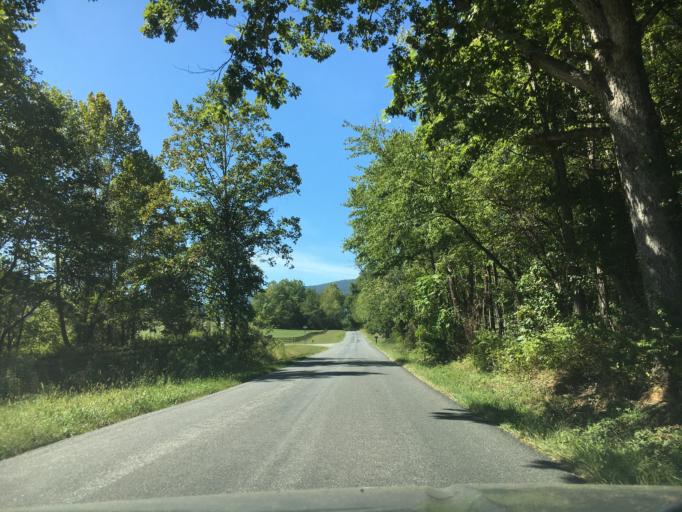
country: US
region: Virginia
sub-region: Albemarle County
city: Crozet
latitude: 38.0266
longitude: -78.7905
